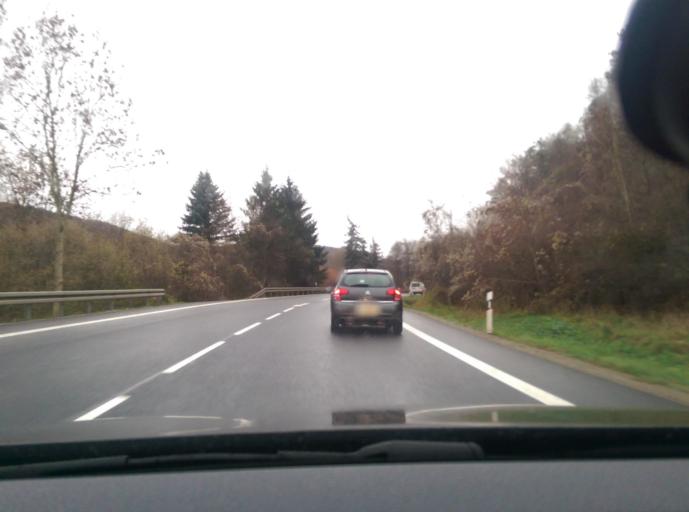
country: DE
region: Hesse
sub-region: Regierungsbezirk Kassel
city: Sontra
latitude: 51.1174
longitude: 9.9757
